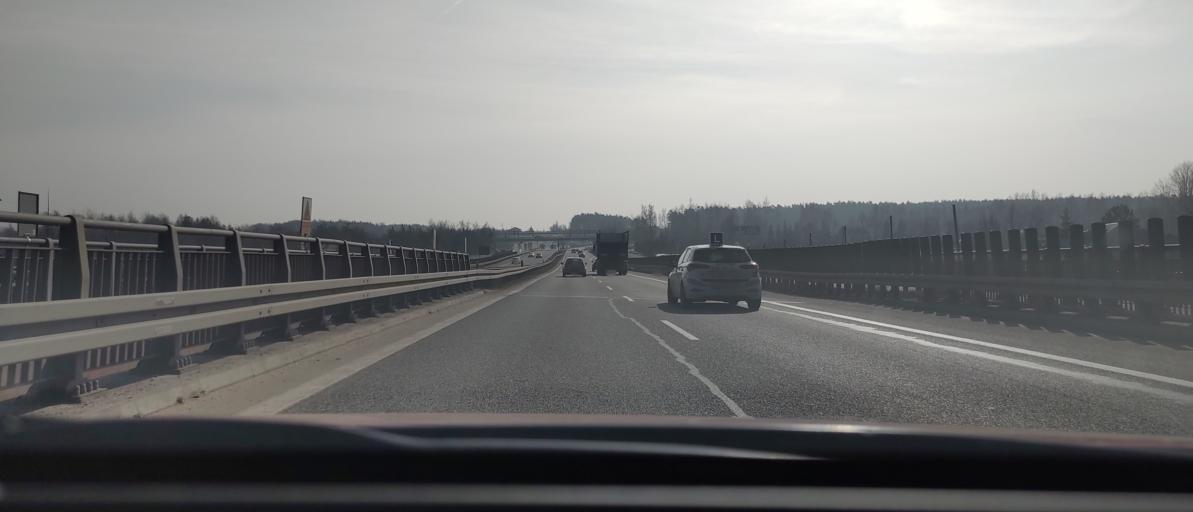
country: PL
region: Masovian Voivodeship
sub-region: Powiat grojecki
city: Grojec
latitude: 51.9038
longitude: 20.8583
